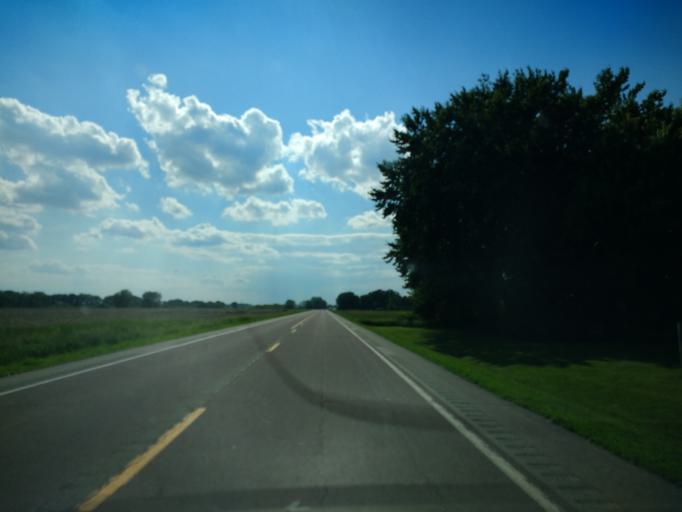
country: US
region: Iowa
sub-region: Clay County
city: Spencer
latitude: 43.1840
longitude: -95.1735
